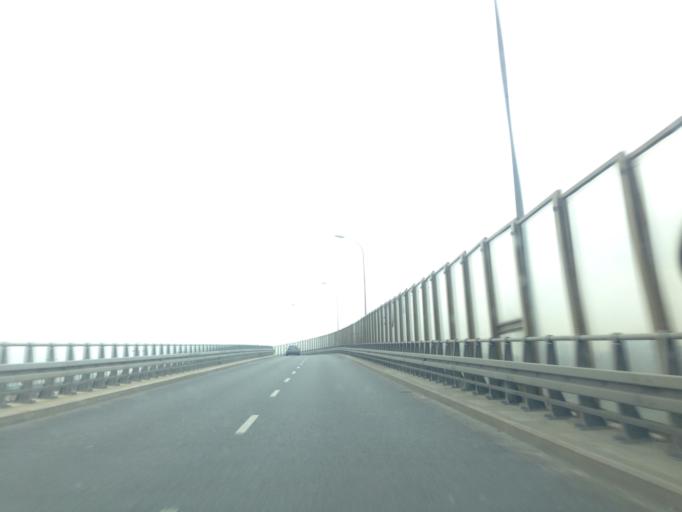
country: PL
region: Masovian Voivodeship
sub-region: Warszawa
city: Mokotow
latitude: 52.1991
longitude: 21.0538
